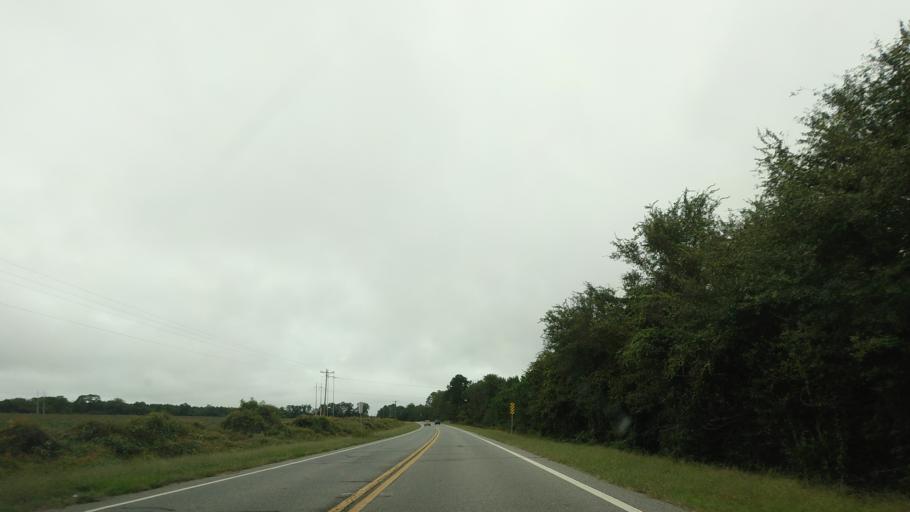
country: US
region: Georgia
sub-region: Irwin County
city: Ocilla
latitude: 31.5342
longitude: -83.2484
